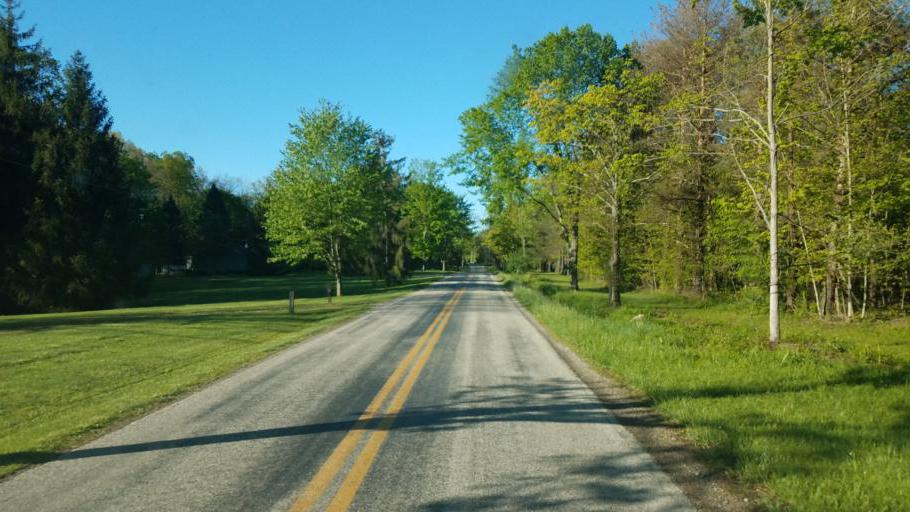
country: US
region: Ohio
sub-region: Delaware County
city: Sunbury
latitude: 40.3476
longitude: -82.8215
